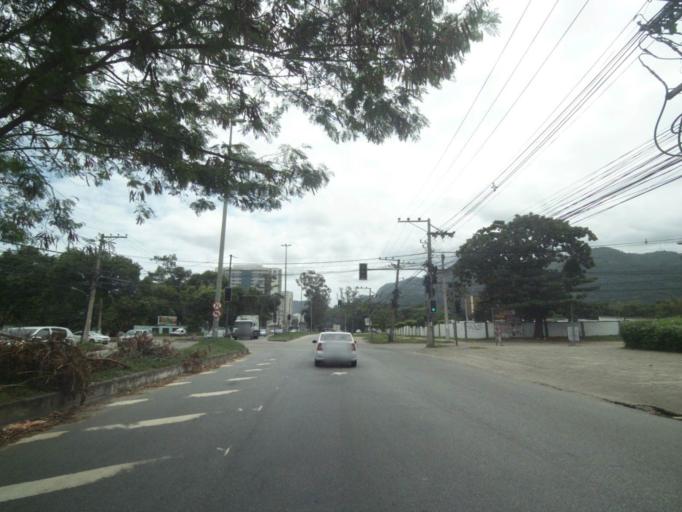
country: BR
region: Rio de Janeiro
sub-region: Nilopolis
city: Nilopolis
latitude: -22.9617
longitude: -43.3968
